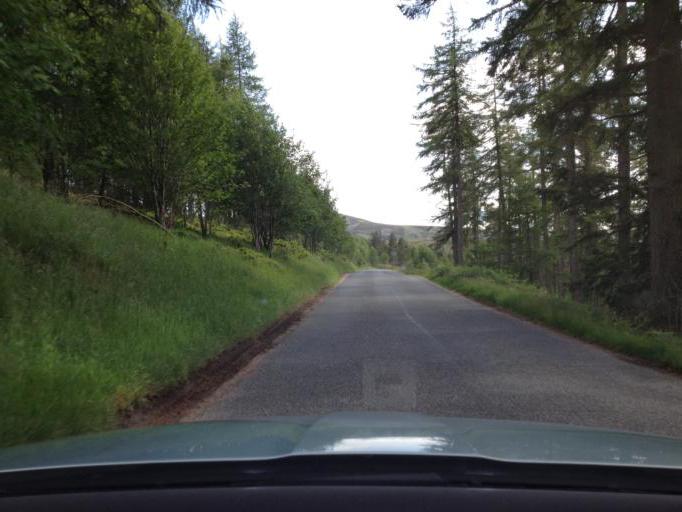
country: GB
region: Scotland
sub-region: Aberdeenshire
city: Banchory
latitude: 56.9550
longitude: -2.5827
